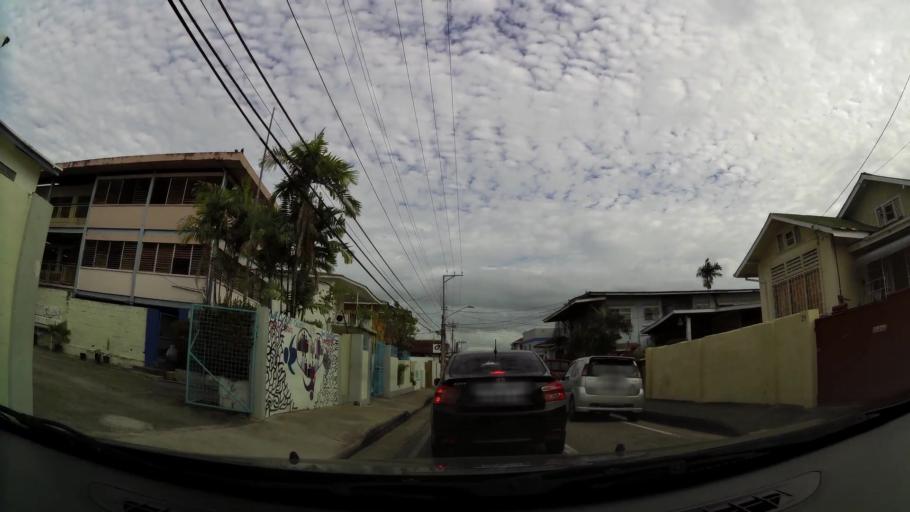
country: TT
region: City of Port of Spain
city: Port-of-Spain
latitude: 10.6613
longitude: -61.5190
